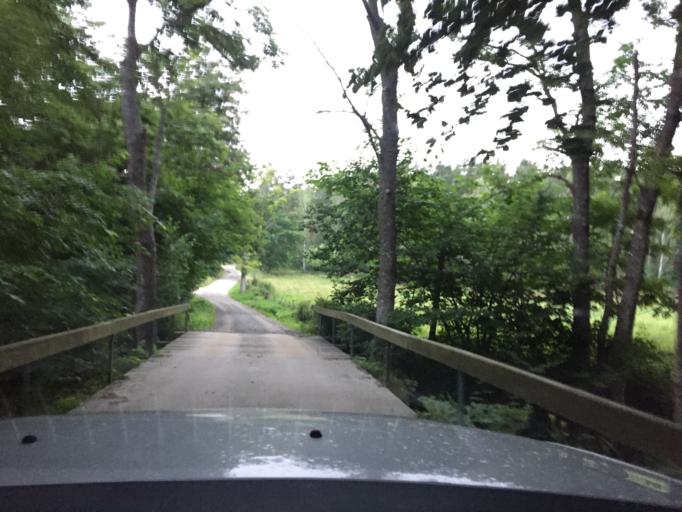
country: SE
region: Skane
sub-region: Kristianstads Kommun
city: Degeberga
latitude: 55.7279
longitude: 14.1252
